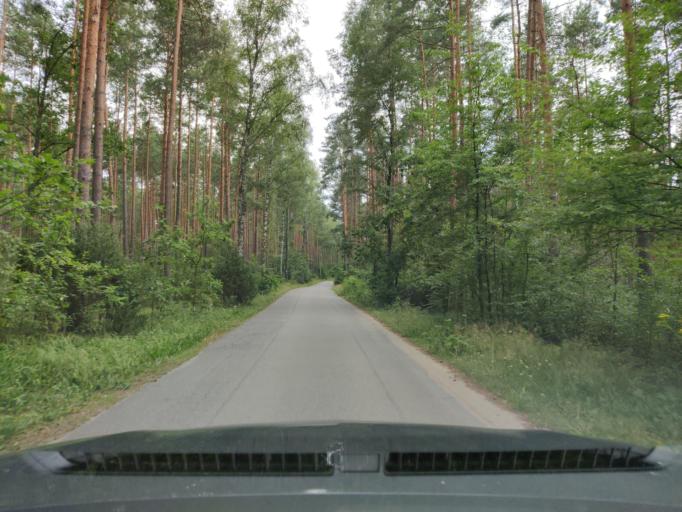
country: PL
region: Masovian Voivodeship
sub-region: Powiat pultuski
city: Pultusk
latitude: 52.7461
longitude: 21.1421
